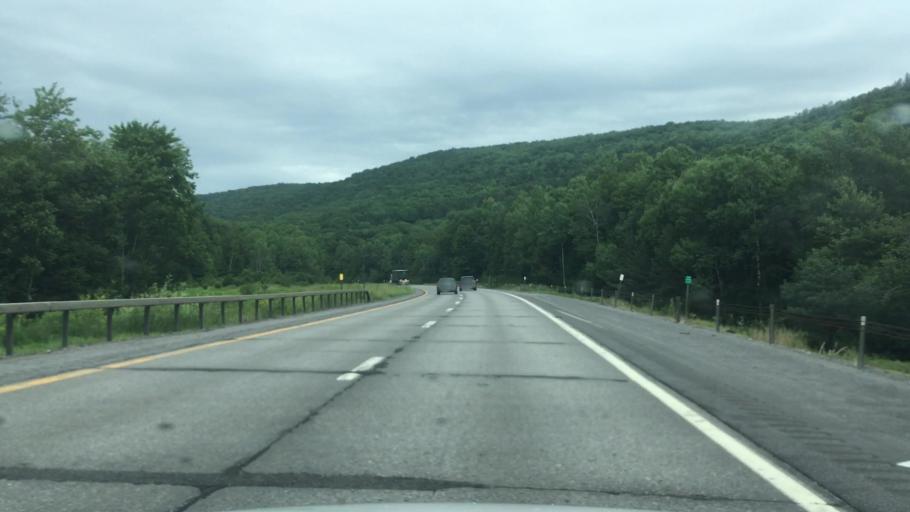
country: US
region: New York
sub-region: Otsego County
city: Worcester
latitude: 42.5940
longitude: -74.7108
